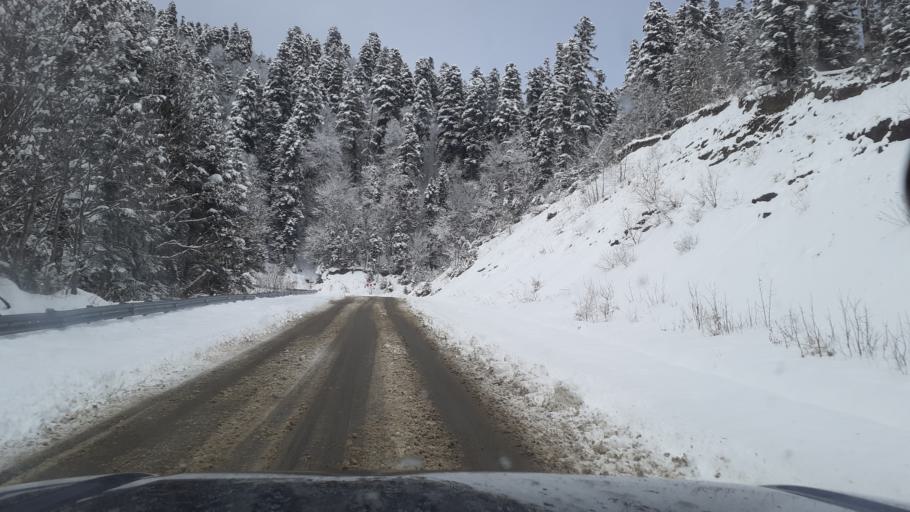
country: RU
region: Adygeya
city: Kamennomostskiy
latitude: 44.0076
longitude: 40.0208
